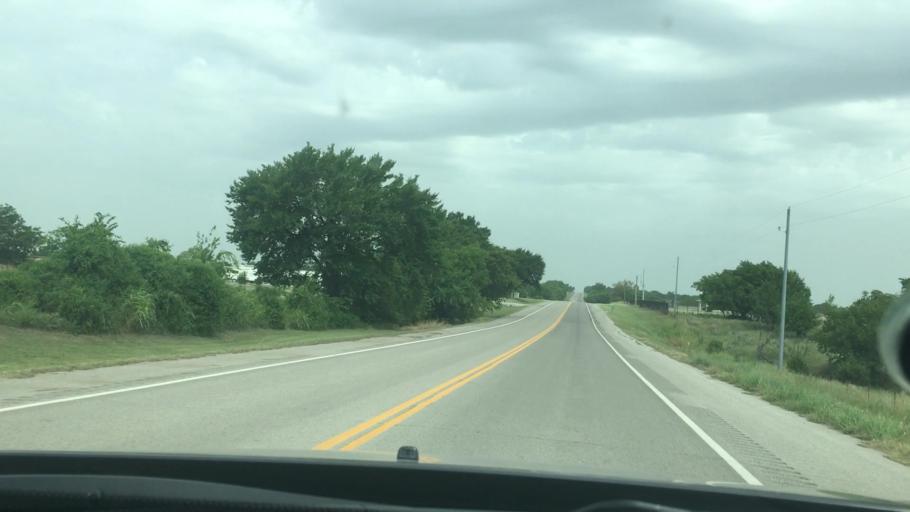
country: US
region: Oklahoma
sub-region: Garvin County
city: Pauls Valley
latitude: 34.8457
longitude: -97.2777
